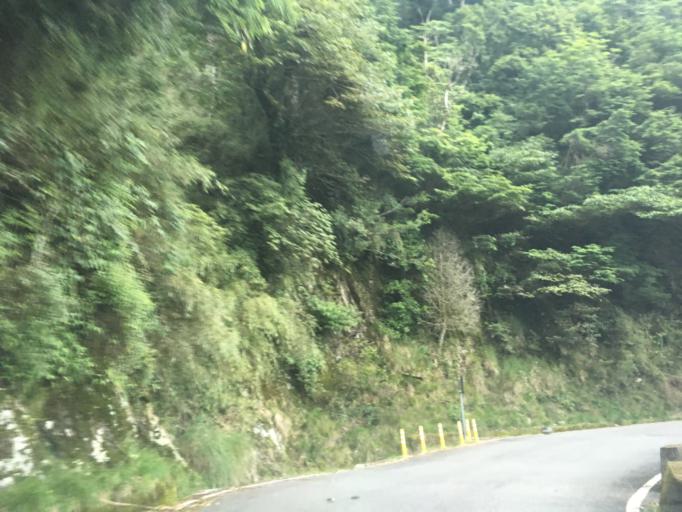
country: TW
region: Taiwan
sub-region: Nantou
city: Puli
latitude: 24.2711
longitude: 121.0277
